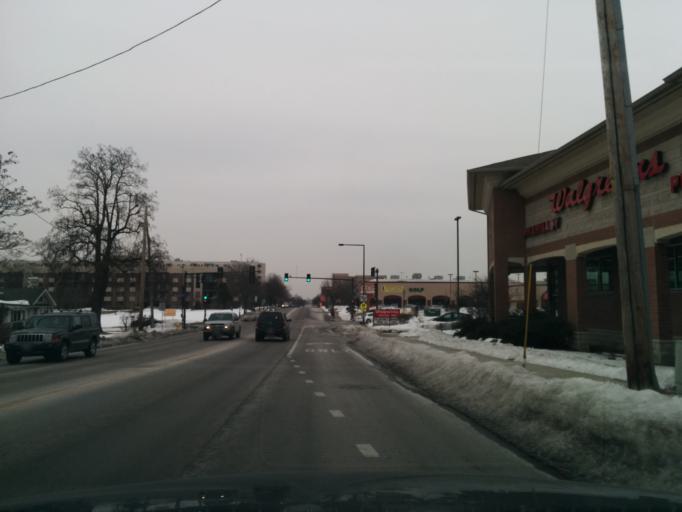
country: US
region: Illinois
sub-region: DuPage County
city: Lombard
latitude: 41.8857
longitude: -88.0248
